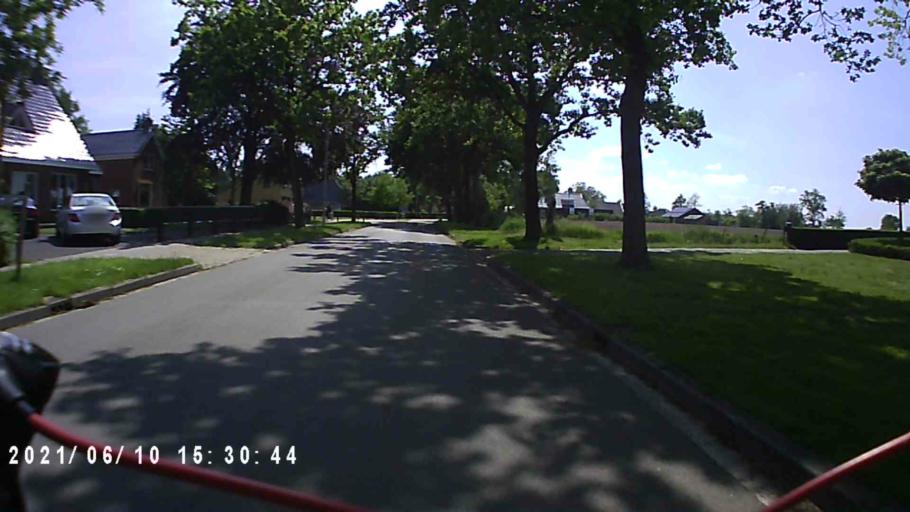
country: NL
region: Friesland
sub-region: Gemeente Achtkarspelen
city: Surhuisterveen
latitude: 53.1769
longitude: 6.1736
